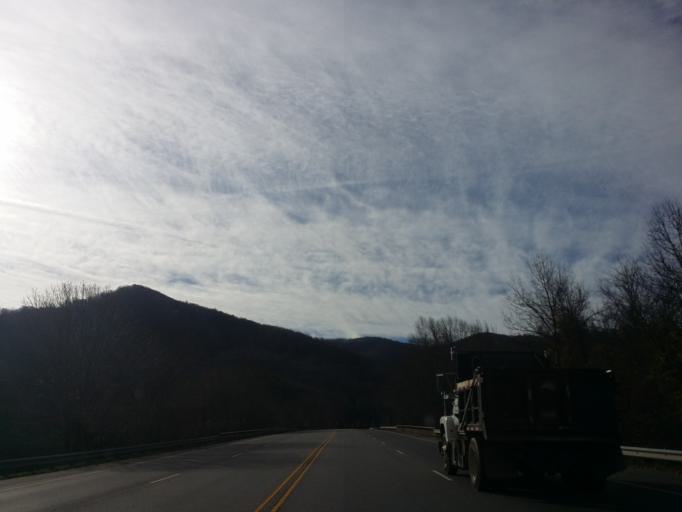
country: US
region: North Carolina
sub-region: Buncombe County
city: Swannanoa
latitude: 35.5971
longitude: -82.4031
